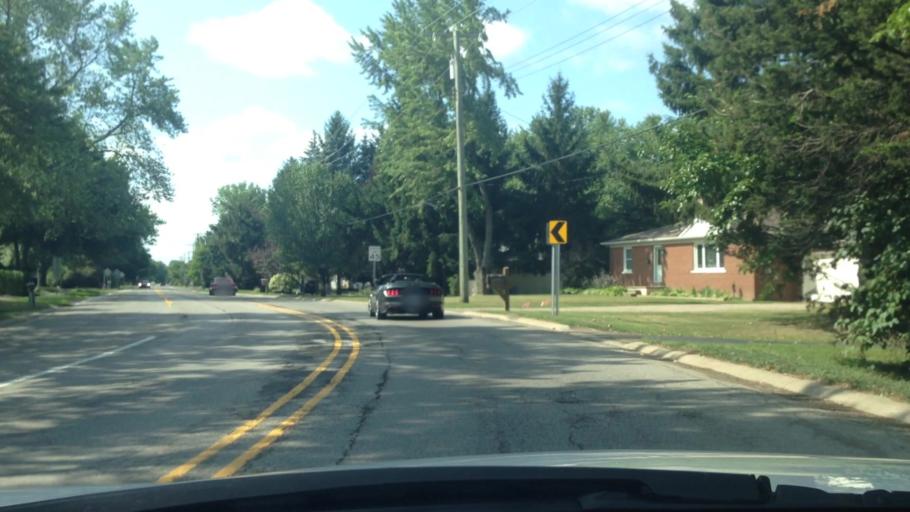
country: US
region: Michigan
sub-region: Oakland County
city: Waterford
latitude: 42.6807
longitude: -83.4317
